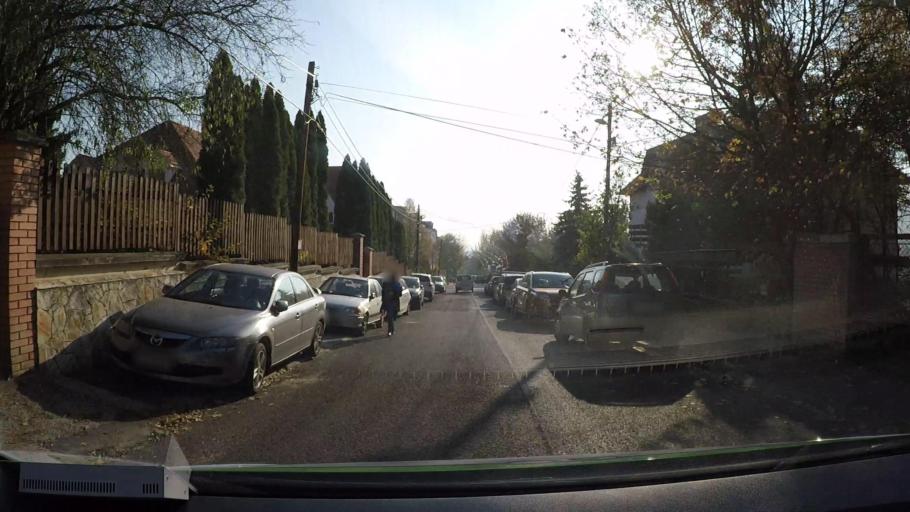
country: HU
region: Pest
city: Budakeszi
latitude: 47.5266
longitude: 18.9758
